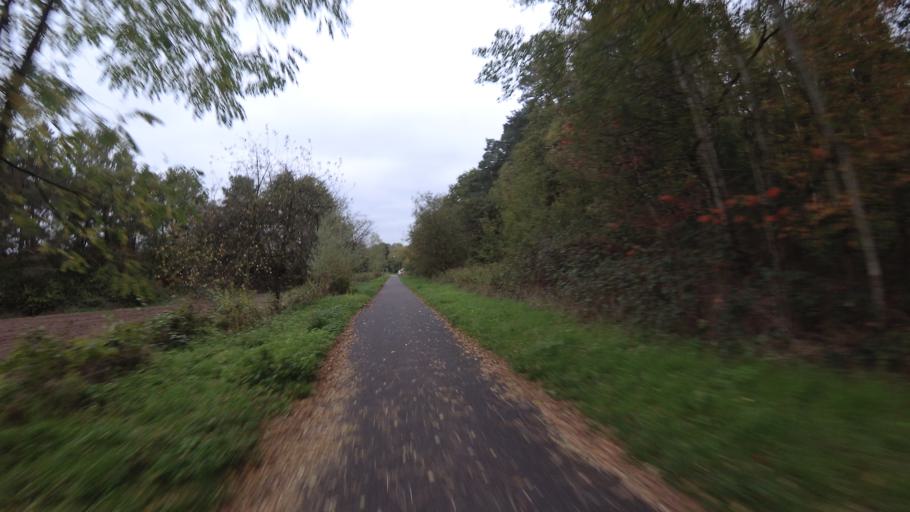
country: DE
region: Saarland
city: Homburg
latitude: 49.2987
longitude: 7.3197
